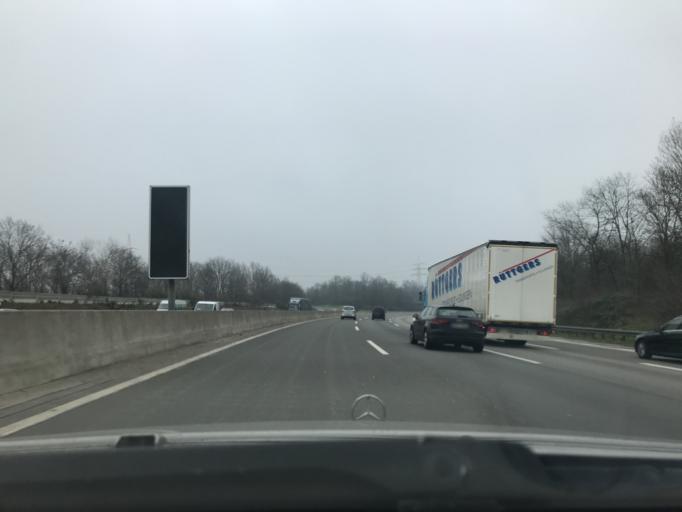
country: DE
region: North Rhine-Westphalia
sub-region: Regierungsbezirk Dusseldorf
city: Dusseldorf
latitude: 51.1884
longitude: 6.7760
